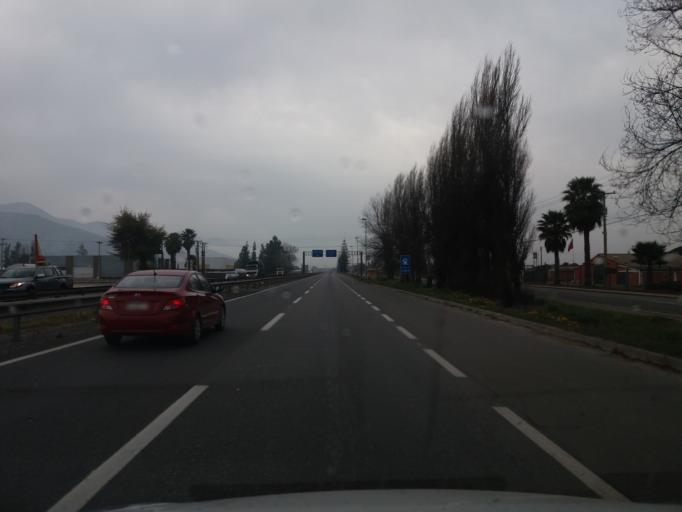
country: CL
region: Valparaiso
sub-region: Provincia de Quillota
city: Hacienda La Calera
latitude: -32.7952
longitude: -71.1608
